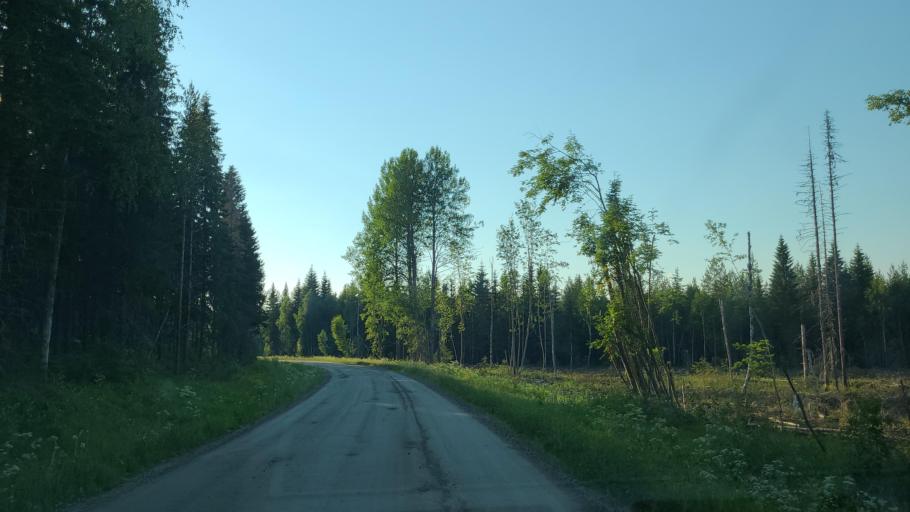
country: SE
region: Vaesterbotten
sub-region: Skelleftea Kommun
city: Burea
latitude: 64.4095
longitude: 21.3564
